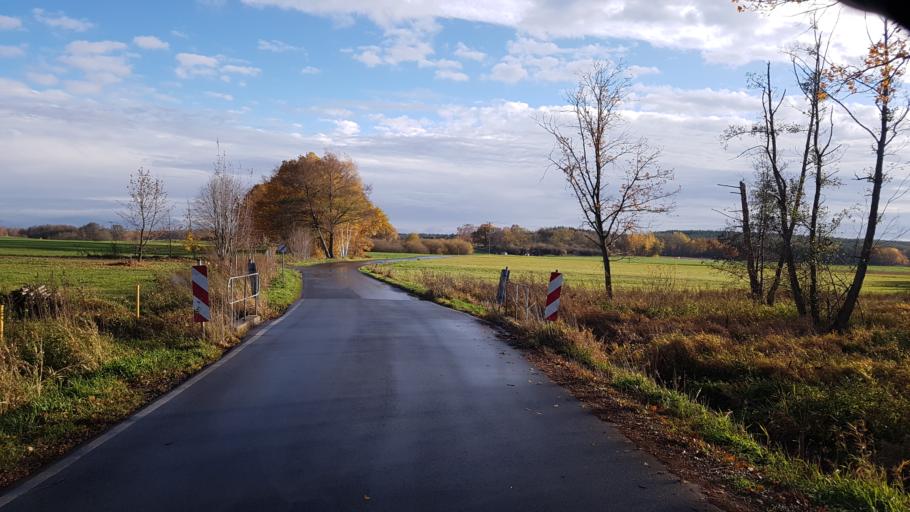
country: DE
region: Brandenburg
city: Ortrand
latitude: 51.3672
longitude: 13.7634
